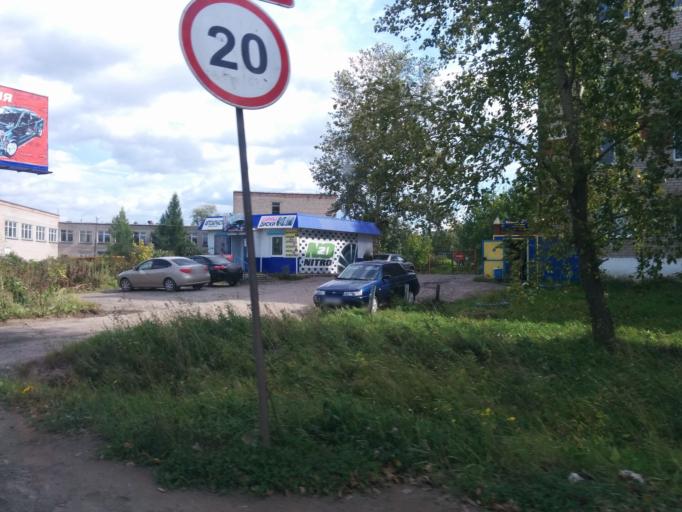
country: RU
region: Perm
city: Kudymkar
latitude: 59.0201
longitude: 54.6644
